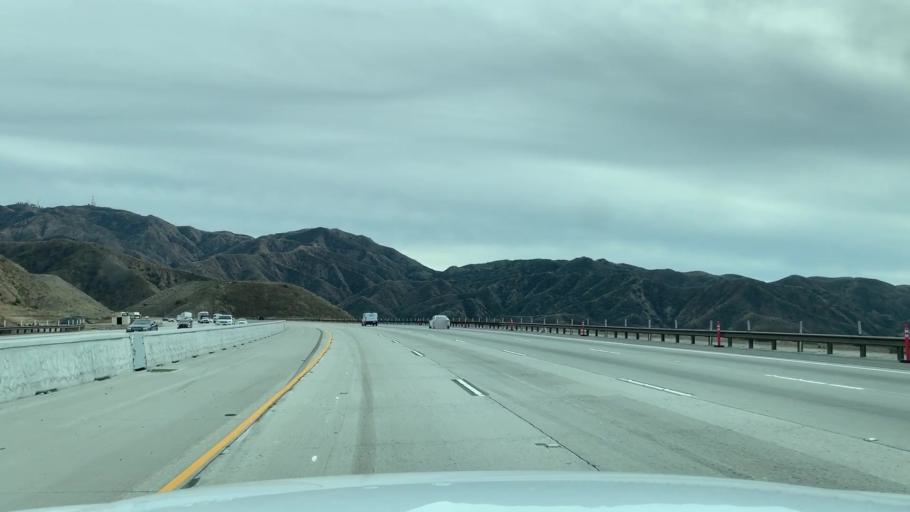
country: US
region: California
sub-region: Los Angeles County
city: Burbank
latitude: 34.2467
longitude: -118.3213
